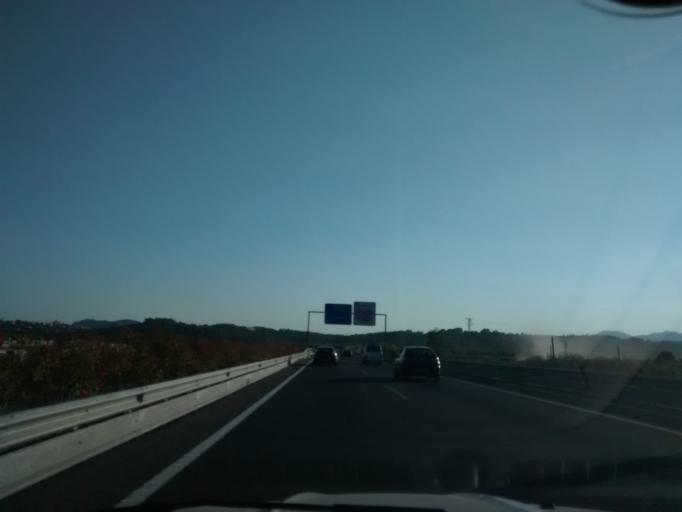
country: ES
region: Balearic Islands
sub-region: Illes Balears
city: sa Pobla
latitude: 39.7845
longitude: 3.0015
